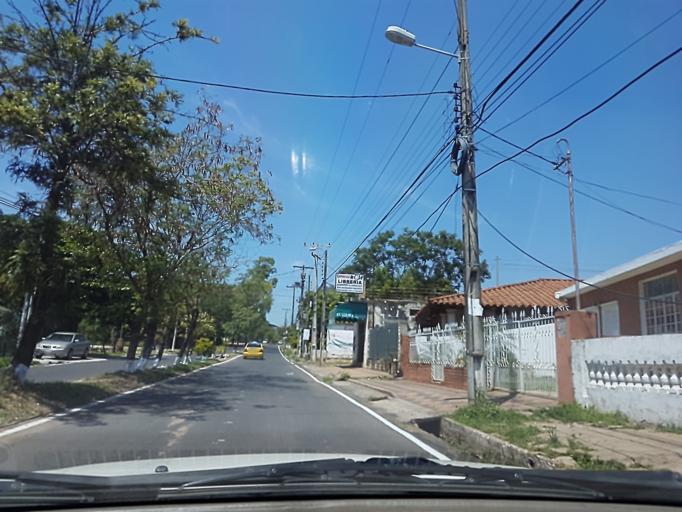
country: PY
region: Central
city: Fernando de la Mora
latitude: -25.2830
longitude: -57.5237
